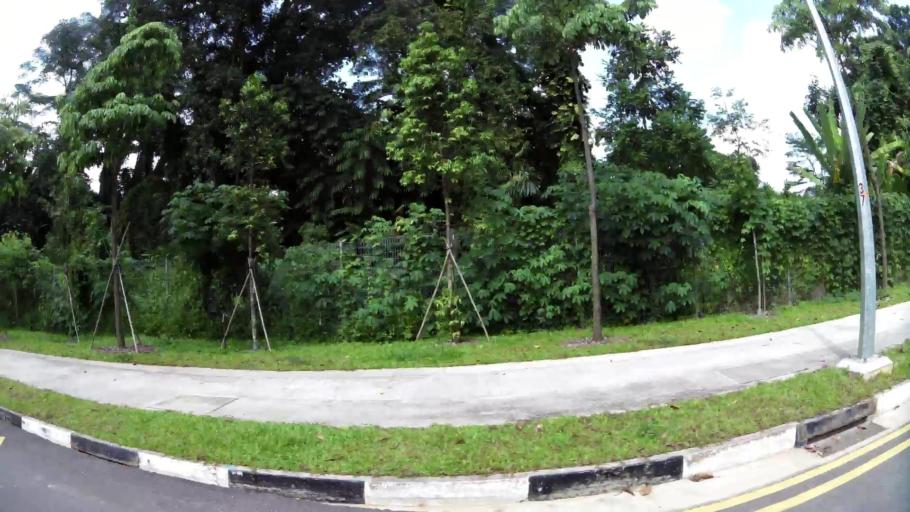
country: SG
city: Singapore
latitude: 1.3126
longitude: 103.8124
